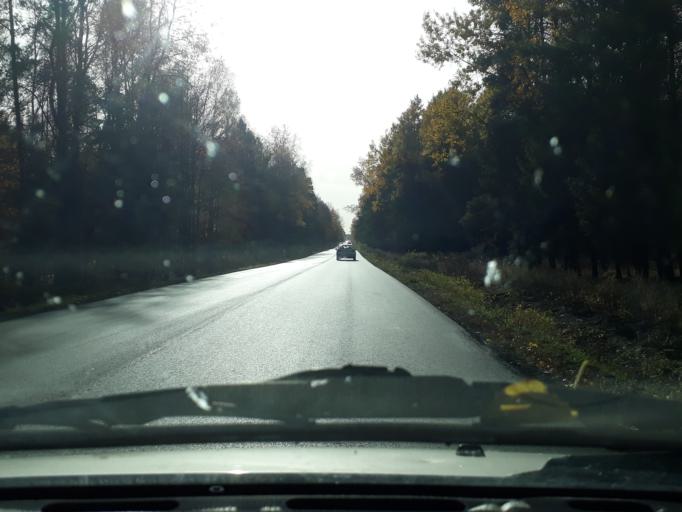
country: PL
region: Silesian Voivodeship
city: Miasteczko Slaskie
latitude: 50.5156
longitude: 18.9503
